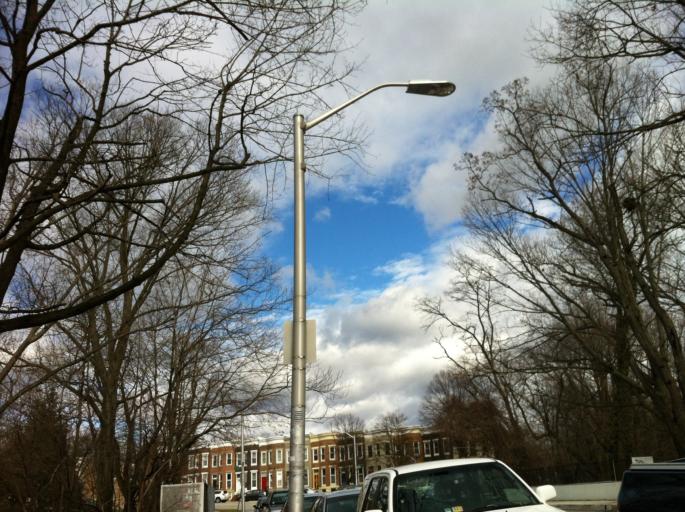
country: US
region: Maryland
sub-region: City of Baltimore
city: Baltimore
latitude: 39.3264
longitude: -76.6256
